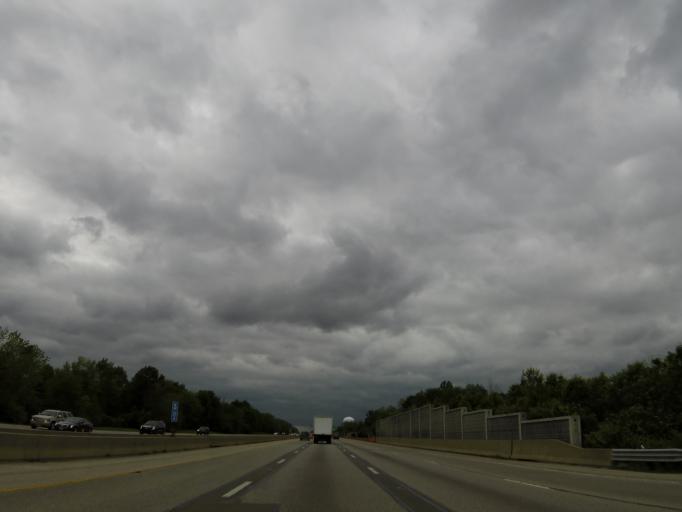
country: US
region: Ohio
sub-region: Warren County
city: Landen
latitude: 39.3114
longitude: -84.2957
